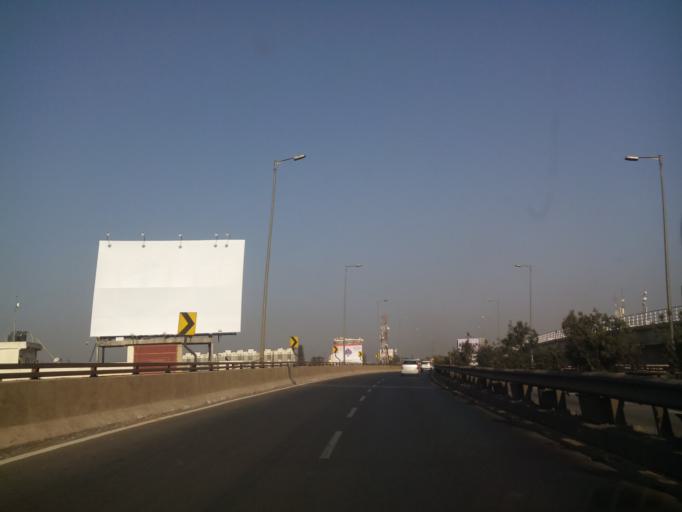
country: IN
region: Karnataka
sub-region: Bangalore Urban
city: Yelahanka
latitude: 13.0433
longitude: 77.5118
